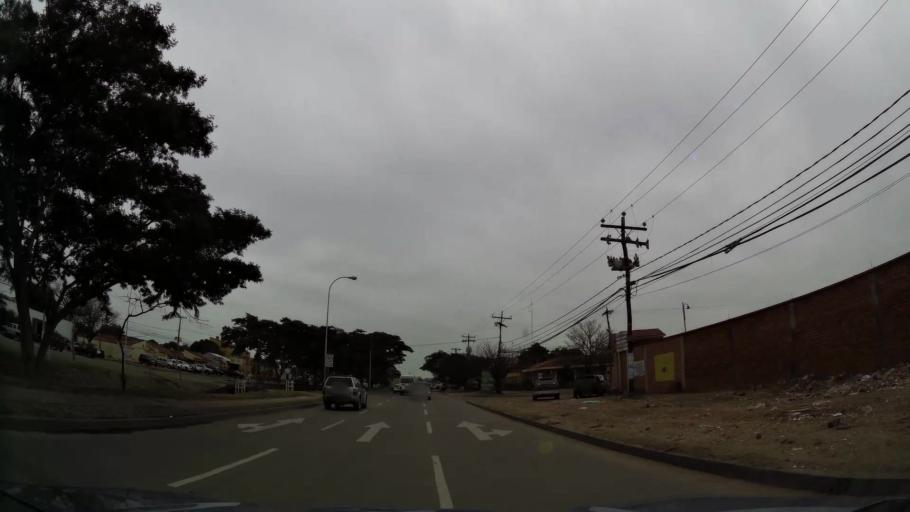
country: BO
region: Santa Cruz
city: Santa Cruz de la Sierra
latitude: -17.7504
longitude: -63.1714
